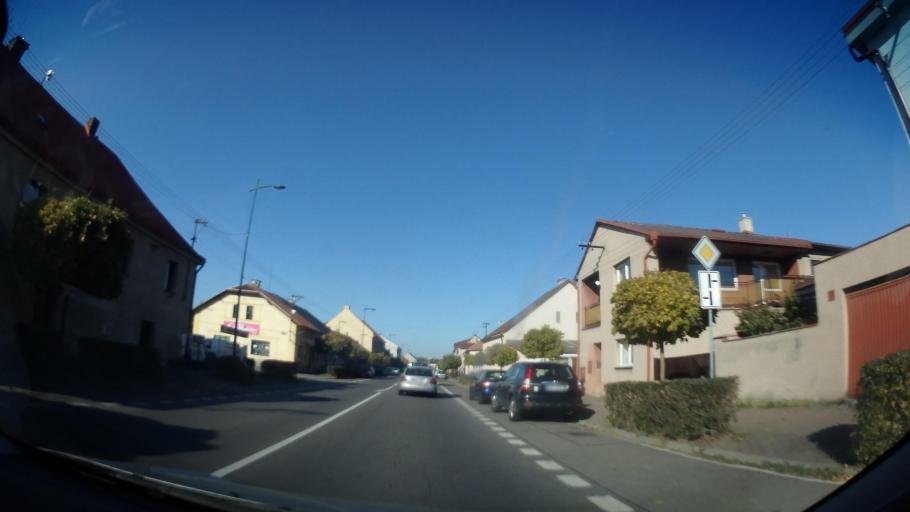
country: CZ
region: Pardubicky
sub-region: Okres Chrudim
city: Slatinany
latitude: 49.9181
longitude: 15.8149
